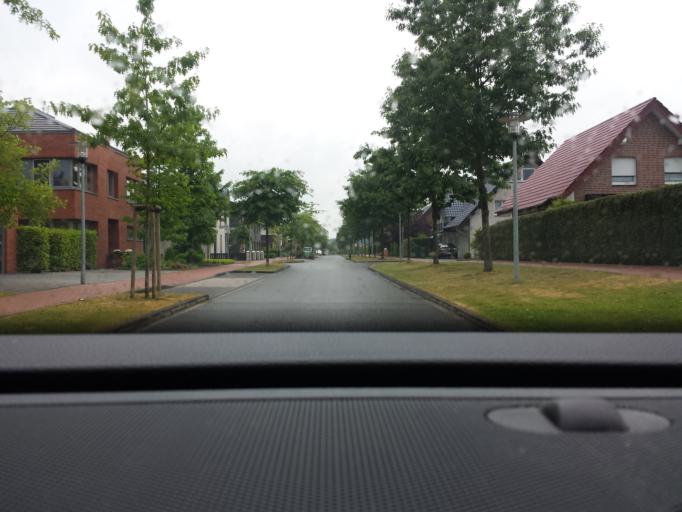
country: DE
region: North Rhine-Westphalia
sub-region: Regierungsbezirk Munster
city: Ahaus
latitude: 52.0729
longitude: 6.9882
